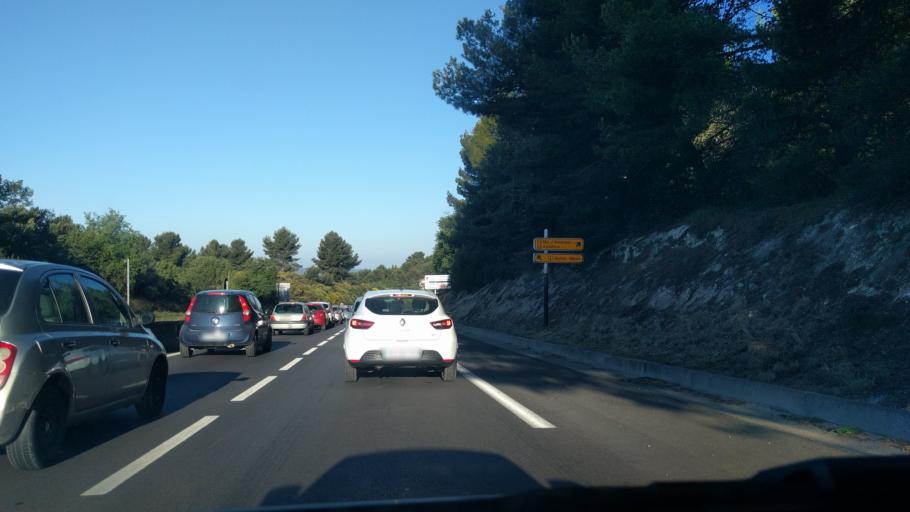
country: FR
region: Provence-Alpes-Cote d'Azur
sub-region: Departement des Bouches-du-Rhone
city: Aix-en-Provence
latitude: 43.5503
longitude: 5.4318
